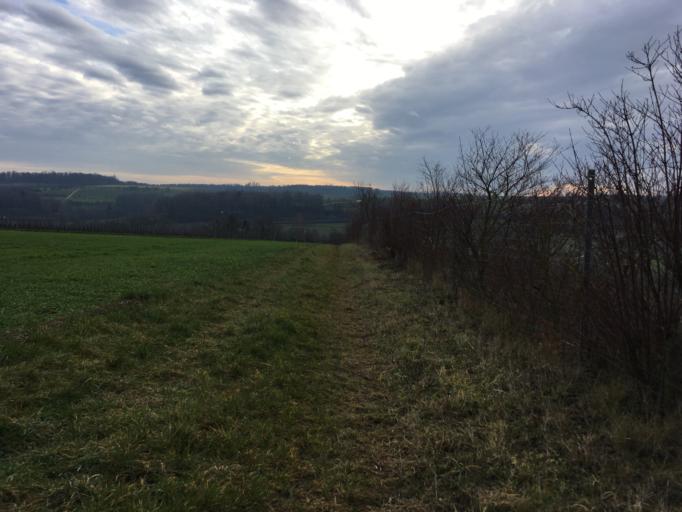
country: DE
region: Baden-Wuerttemberg
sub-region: Regierungsbezirk Stuttgart
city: Ilsfeld
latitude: 49.0582
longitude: 9.2182
